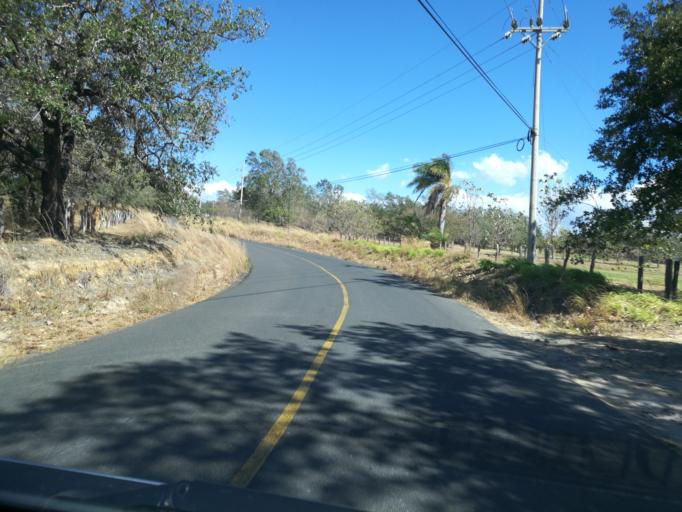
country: CR
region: Guanacaste
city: Liberia
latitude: 10.6653
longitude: -85.4652
